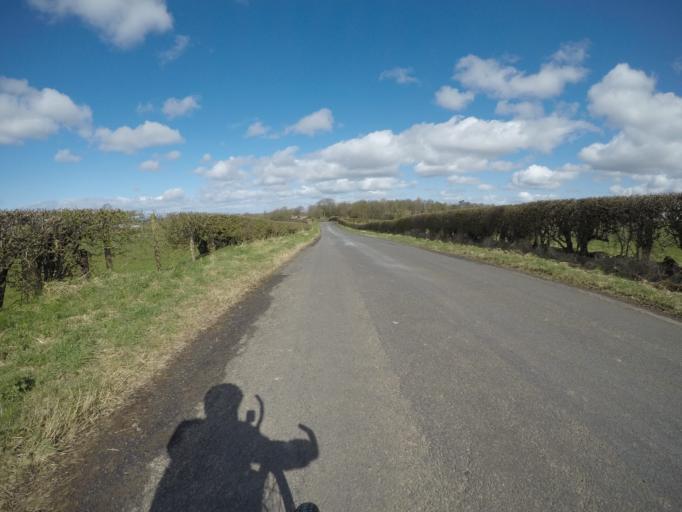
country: GB
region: Scotland
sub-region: East Ayrshire
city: Crosshouse
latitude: 55.6083
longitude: -4.5758
